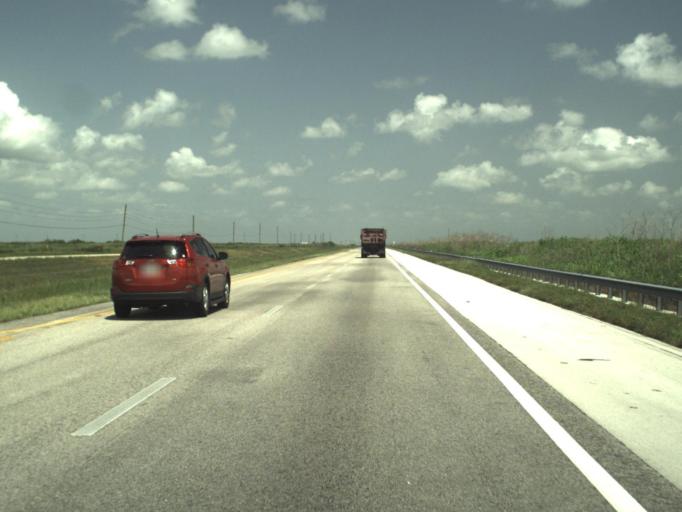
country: US
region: Florida
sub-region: Broward County
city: Coral Springs
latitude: 26.3559
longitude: -80.5539
